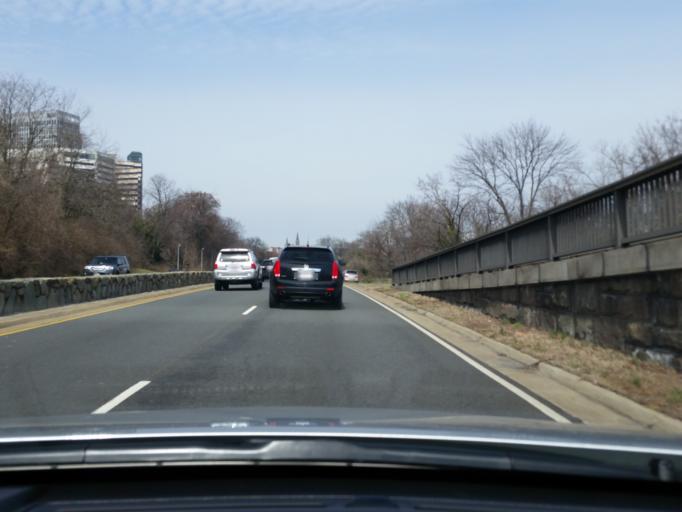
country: US
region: Washington, D.C.
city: Washington, D.C.
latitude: 38.8936
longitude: -77.0657
